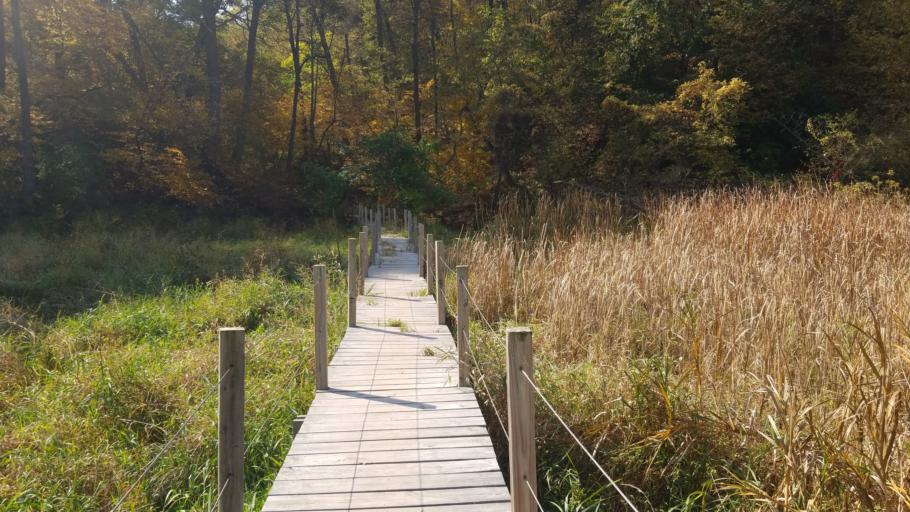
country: US
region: Nebraska
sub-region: Sarpy County
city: Bellevue
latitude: 41.1804
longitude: -95.9003
